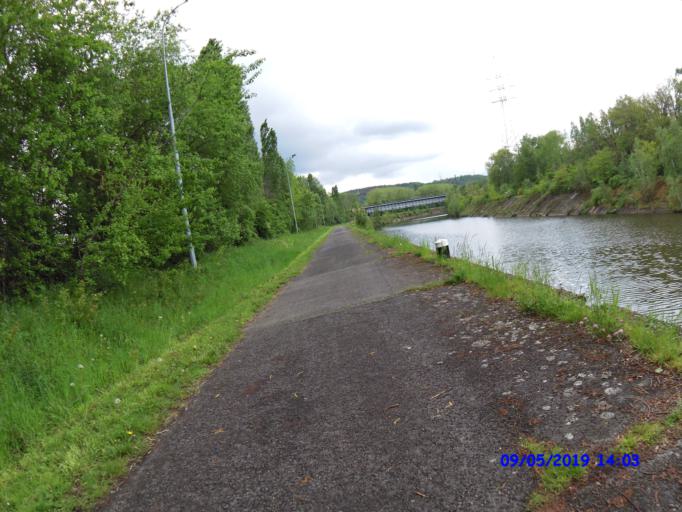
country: BE
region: Wallonia
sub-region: Province du Hainaut
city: Farciennes
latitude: 50.4303
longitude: 4.5574
